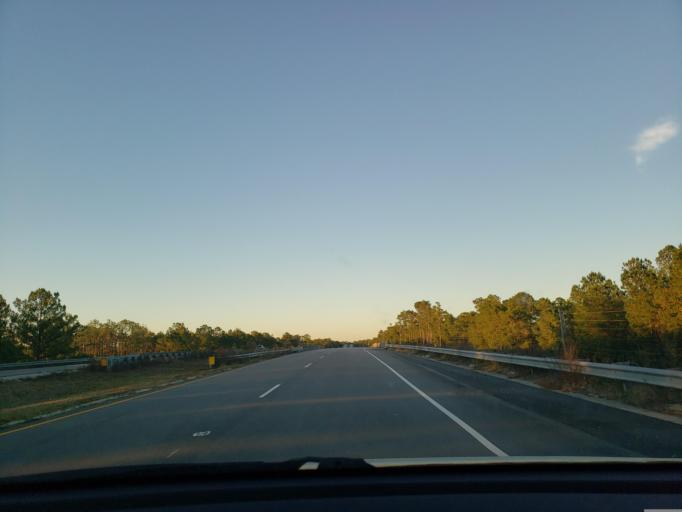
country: US
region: North Carolina
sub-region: Onslow County
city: Sneads Ferry
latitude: 34.5940
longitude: -77.4804
